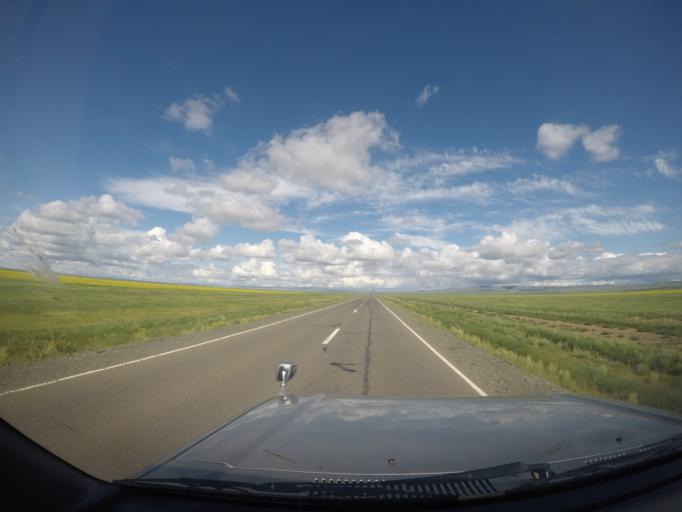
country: MN
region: Hentiy
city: Moron
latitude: 47.4187
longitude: 109.9518
